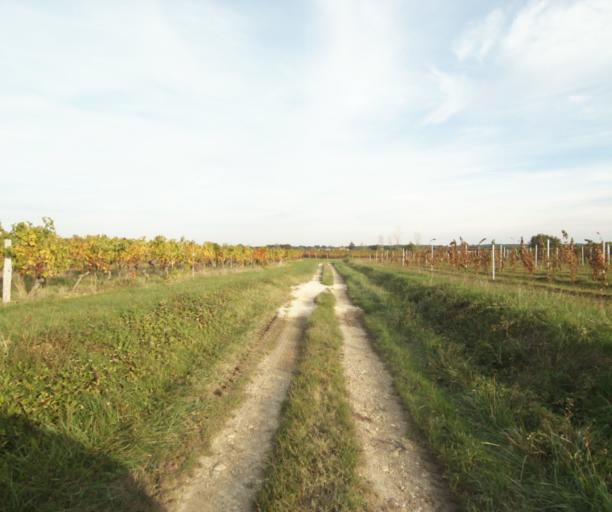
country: FR
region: Midi-Pyrenees
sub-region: Departement du Tarn-et-Garonne
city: Campsas
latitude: 43.8876
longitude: 1.3375
